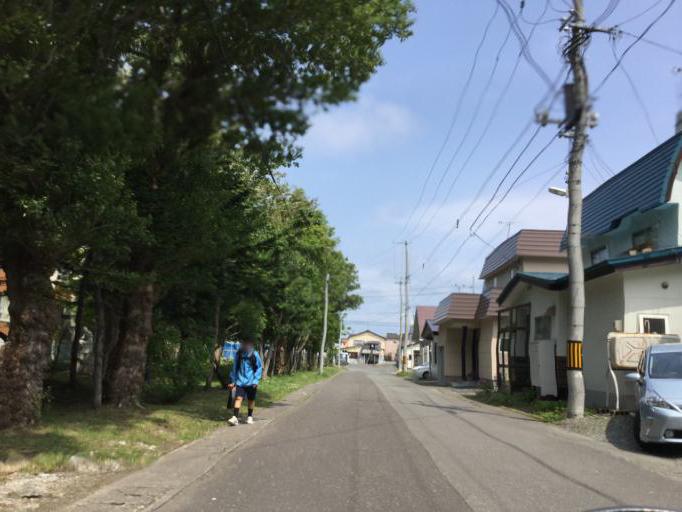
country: JP
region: Hokkaido
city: Wakkanai
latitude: 45.4302
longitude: 141.6664
